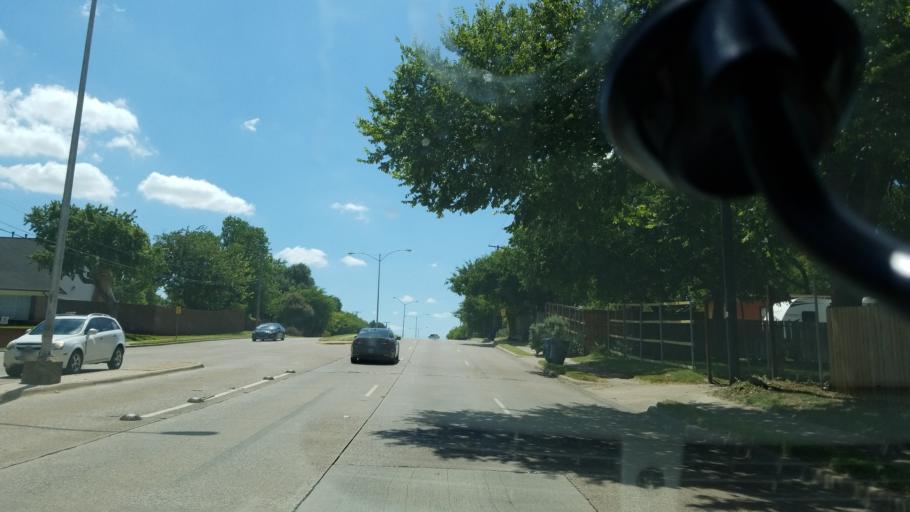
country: US
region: Texas
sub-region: Dallas County
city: Cockrell Hill
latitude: 32.7059
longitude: -96.8450
